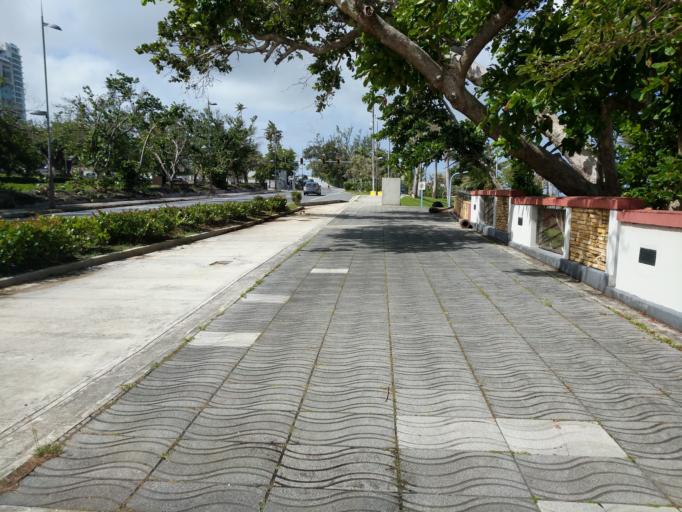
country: PR
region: San Juan
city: San Juan
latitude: 18.4658
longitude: -66.0920
